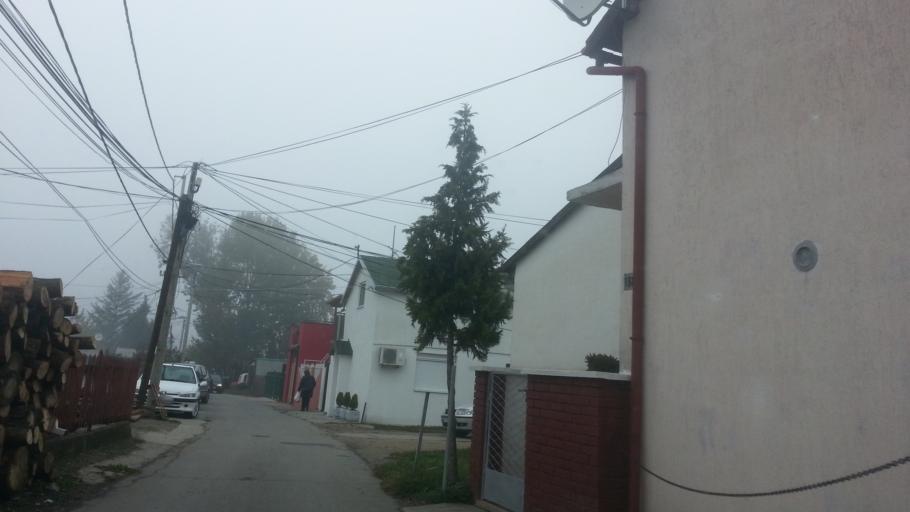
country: RS
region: Central Serbia
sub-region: Belgrade
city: Zemun
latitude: 44.8605
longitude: 20.3799
